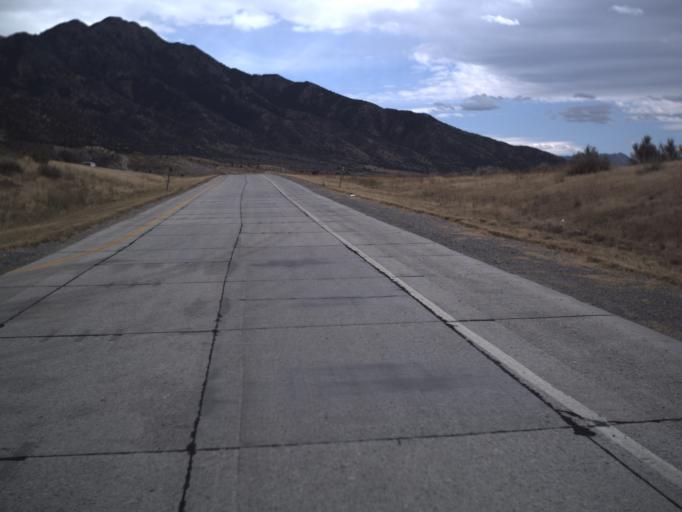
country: US
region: Idaho
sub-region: Oneida County
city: Malad City
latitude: 41.9767
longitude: -112.1907
